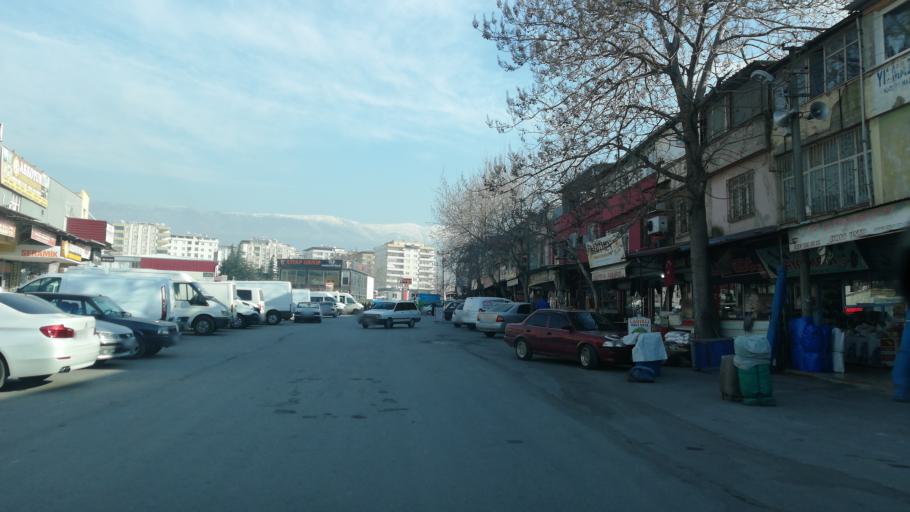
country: TR
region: Kahramanmaras
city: Kahramanmaras
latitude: 37.5672
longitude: 36.9176
